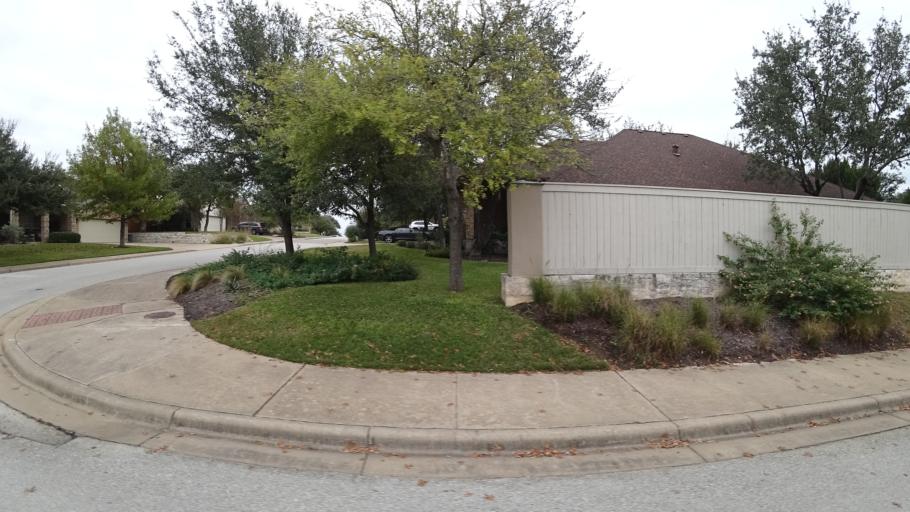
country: US
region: Texas
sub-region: Travis County
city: Bee Cave
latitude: 30.3164
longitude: -97.9175
